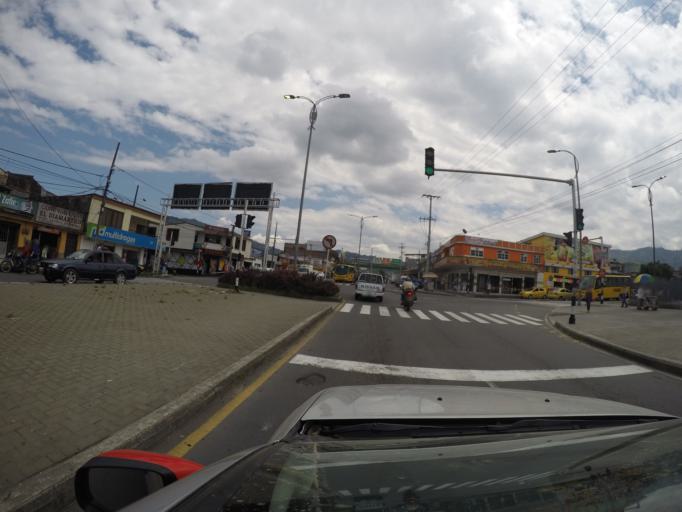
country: CO
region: Risaralda
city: Dos Quebradas
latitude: 4.8365
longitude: -75.6694
